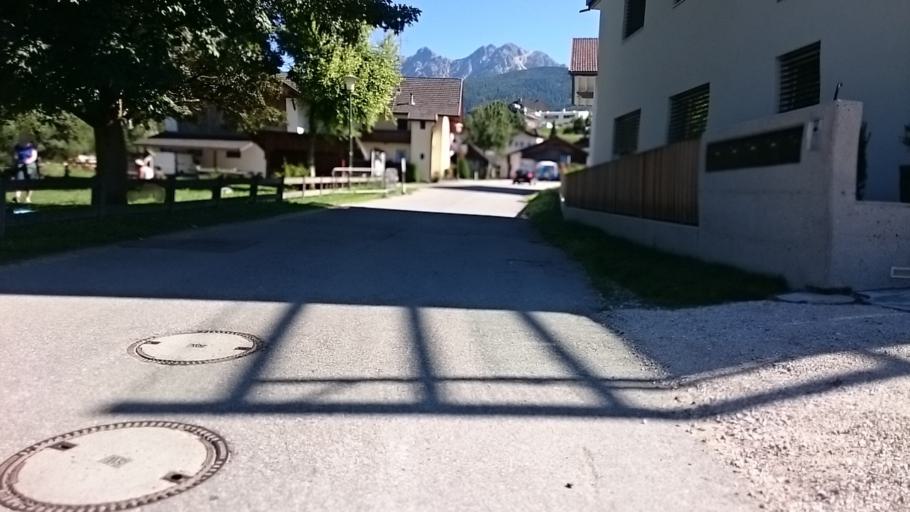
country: IT
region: Trentino-Alto Adige
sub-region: Bolzano
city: Valdaora di Mezzo
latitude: 46.7706
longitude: 12.0169
